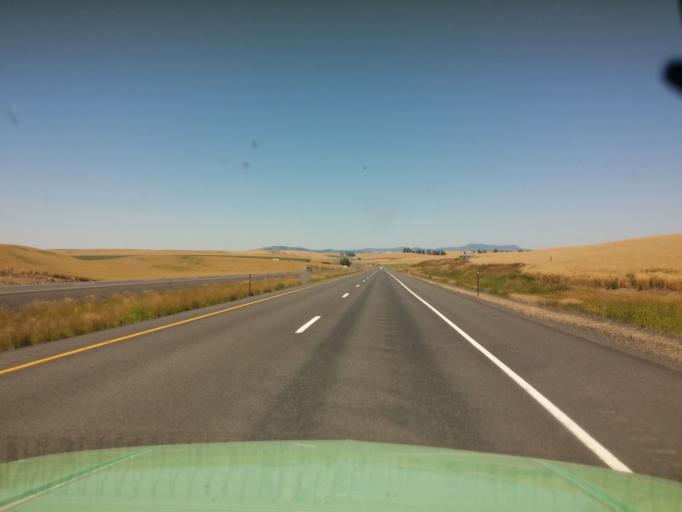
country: US
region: Idaho
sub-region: Nez Perce County
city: Lewiston
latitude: 46.5255
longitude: -116.9486
